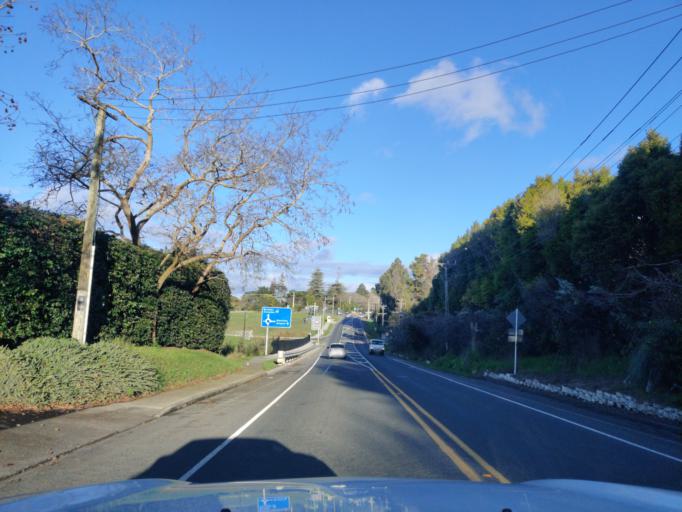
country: NZ
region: Auckland
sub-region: Auckland
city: Pakuranga
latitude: -36.9484
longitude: 174.9647
